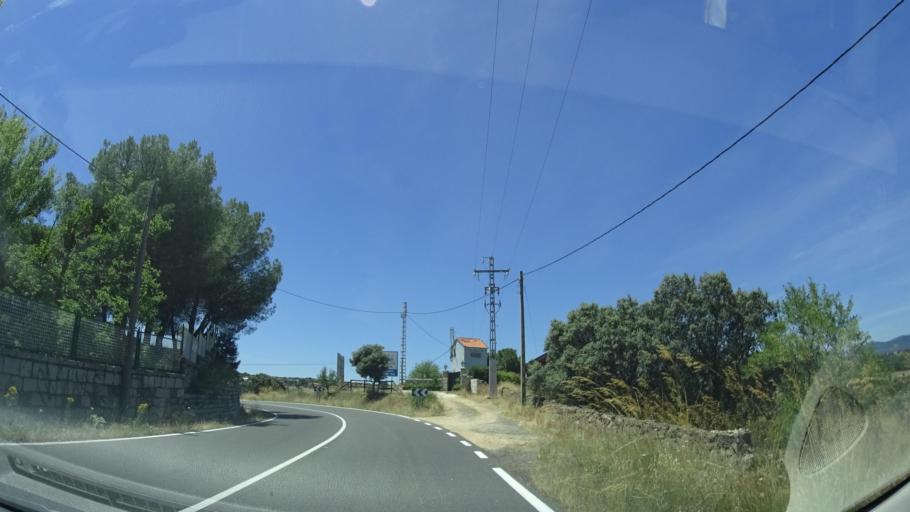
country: ES
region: Madrid
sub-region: Provincia de Madrid
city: Galapagar
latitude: 40.6051
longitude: -3.9833
